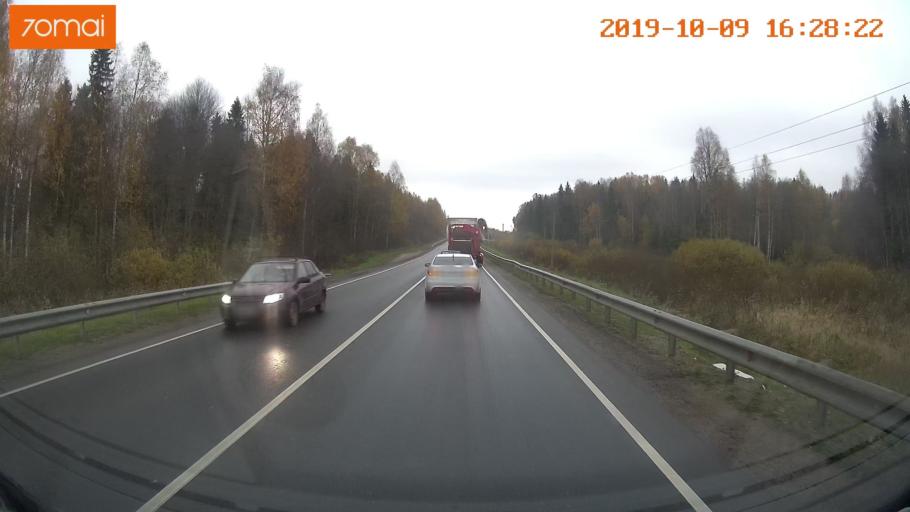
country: RU
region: Kostroma
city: Oktyabr'skiy
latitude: 57.6291
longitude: 40.9317
